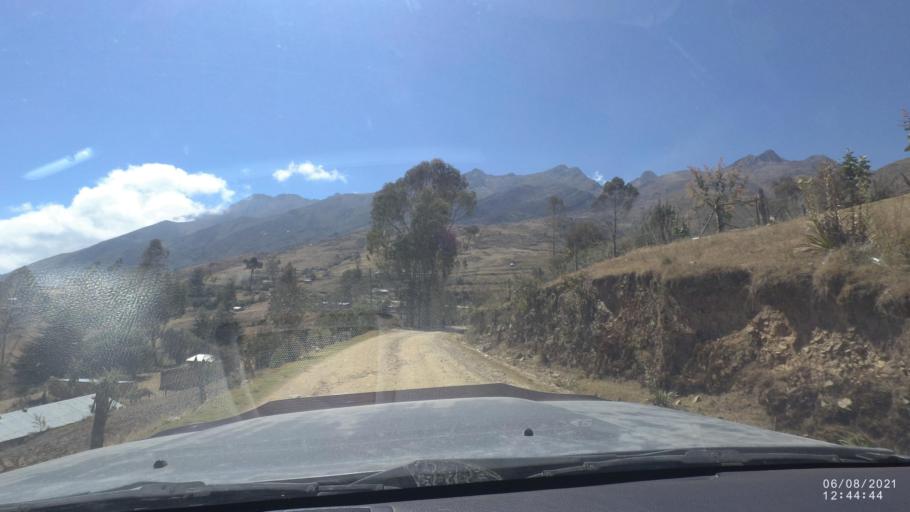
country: BO
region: Cochabamba
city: Colchani
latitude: -16.7676
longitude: -66.6649
